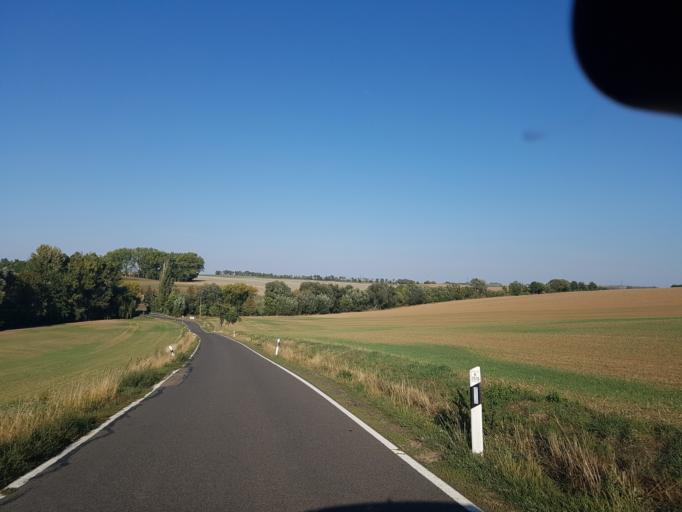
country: DE
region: Saxony
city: Ostrau
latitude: 51.1943
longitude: 13.1199
